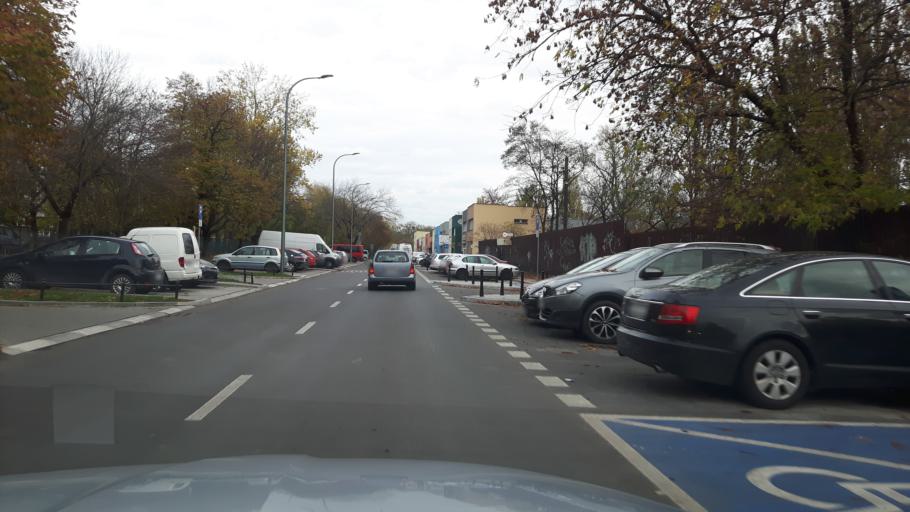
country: PL
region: Masovian Voivodeship
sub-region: Warszawa
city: Mokotow
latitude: 52.1684
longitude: 21.0025
